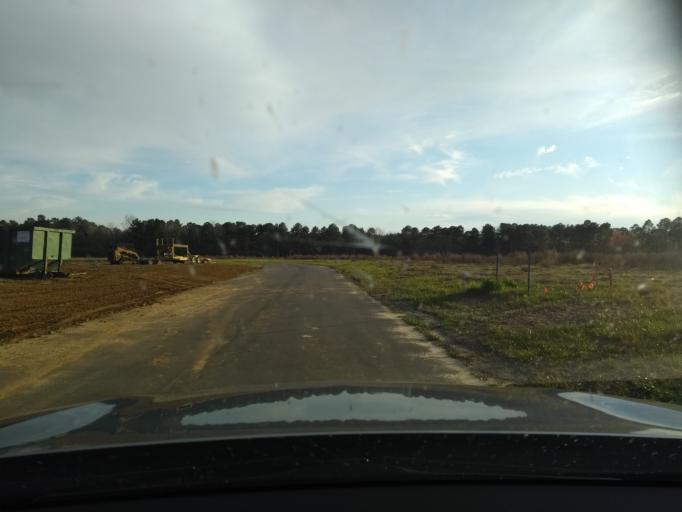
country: US
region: Georgia
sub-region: Bulloch County
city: Statesboro
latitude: 32.3577
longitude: -81.7677
